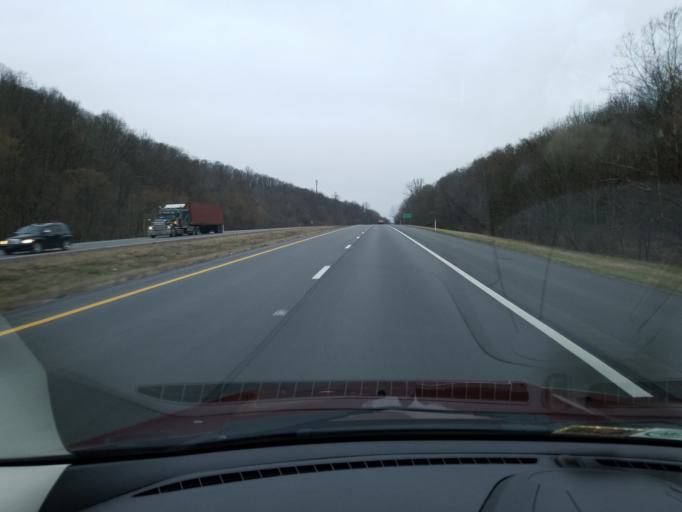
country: US
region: Virginia
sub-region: Giles County
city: Narrows
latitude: 37.3616
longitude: -80.8780
